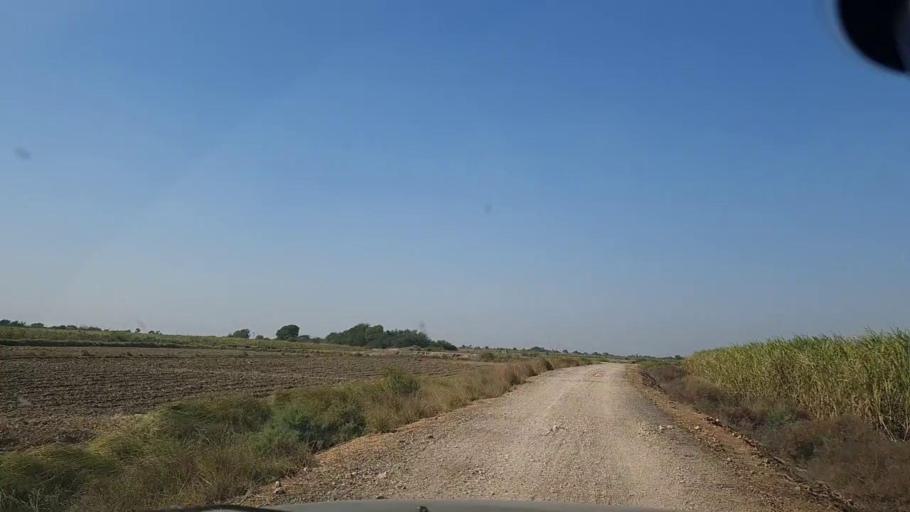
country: PK
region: Sindh
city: Chuhar Jamali
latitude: 24.5754
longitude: 68.0405
